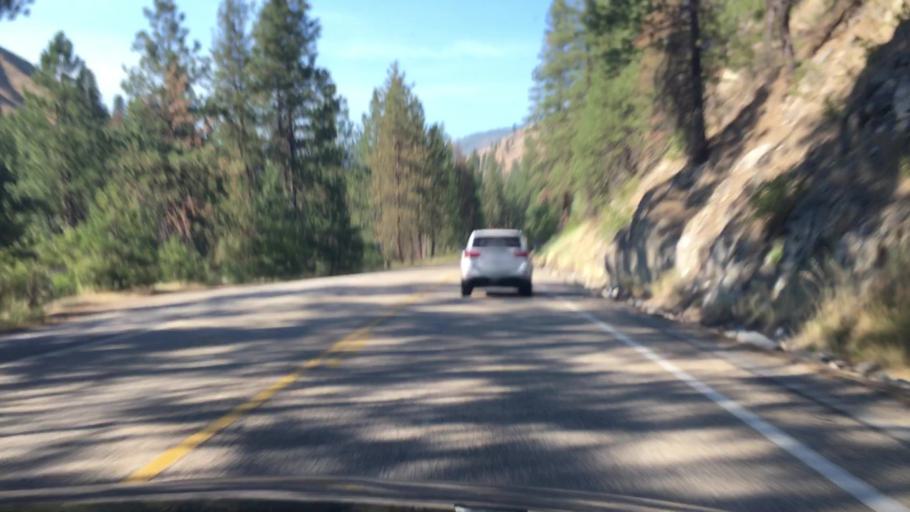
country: US
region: Idaho
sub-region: Boise County
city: Idaho City
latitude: 44.0580
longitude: -116.1265
